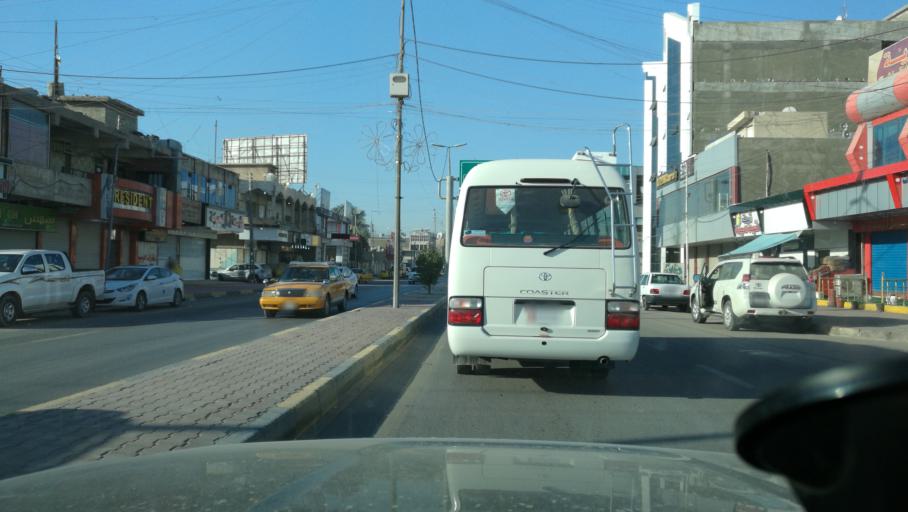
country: IQ
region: Basra Governorate
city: Al Basrah al Qadimah
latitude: 30.5051
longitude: 47.8335
